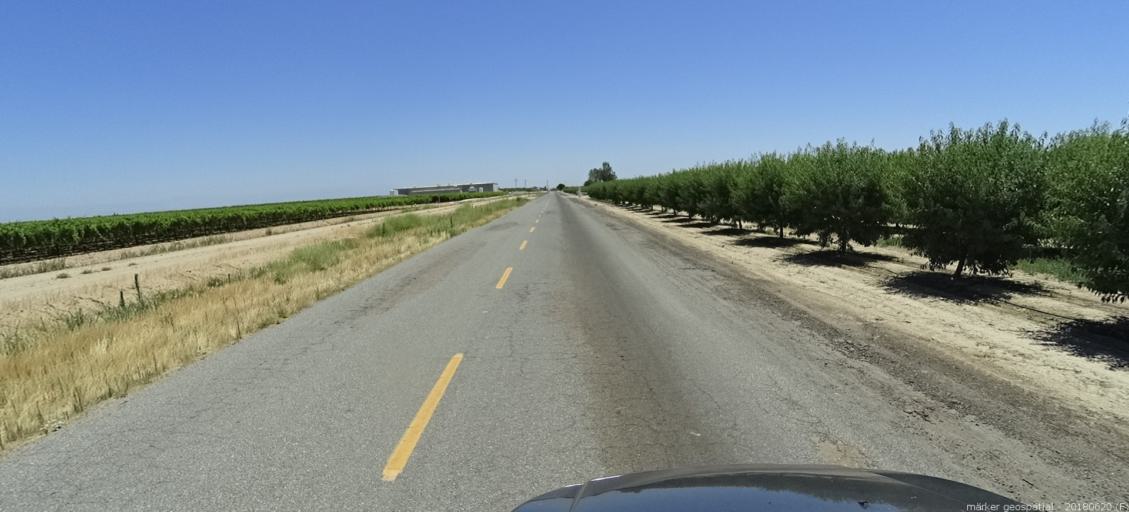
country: US
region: California
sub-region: Fresno County
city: Biola
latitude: 36.8658
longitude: -119.9893
